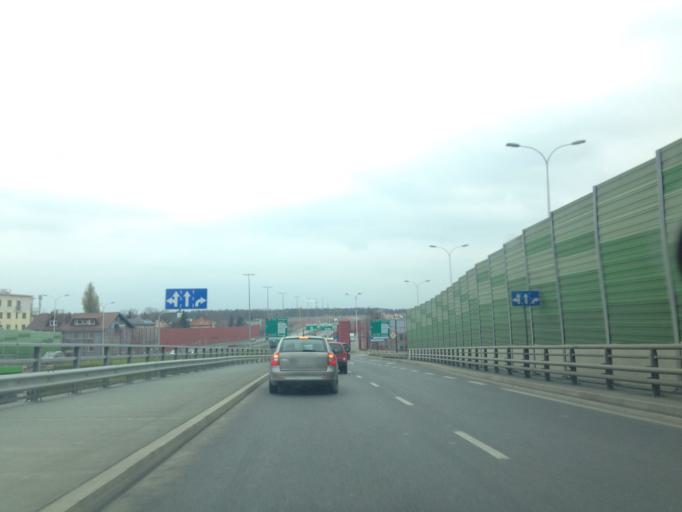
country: PL
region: Masovian Voivodeship
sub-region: Warszawa
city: Rembertow
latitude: 52.2386
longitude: 21.1314
